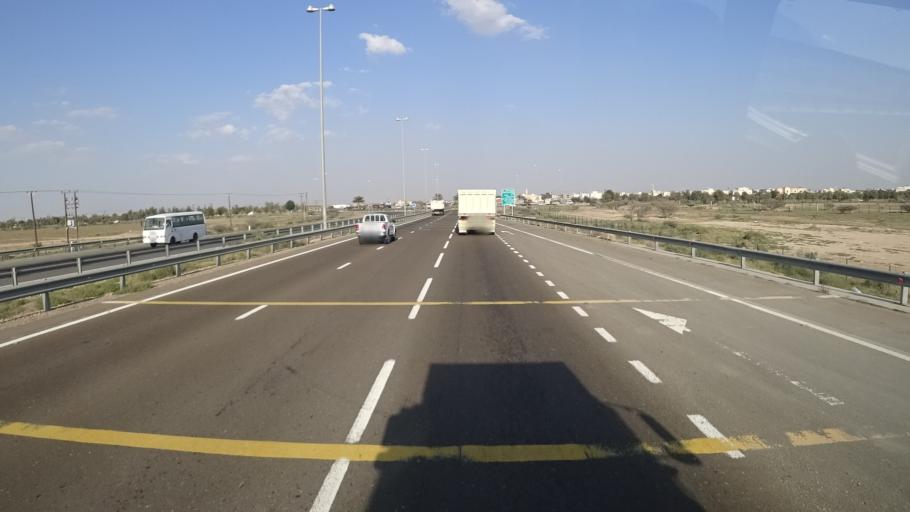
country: AE
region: Abu Dhabi
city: Al Ain
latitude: 24.1095
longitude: 55.8225
